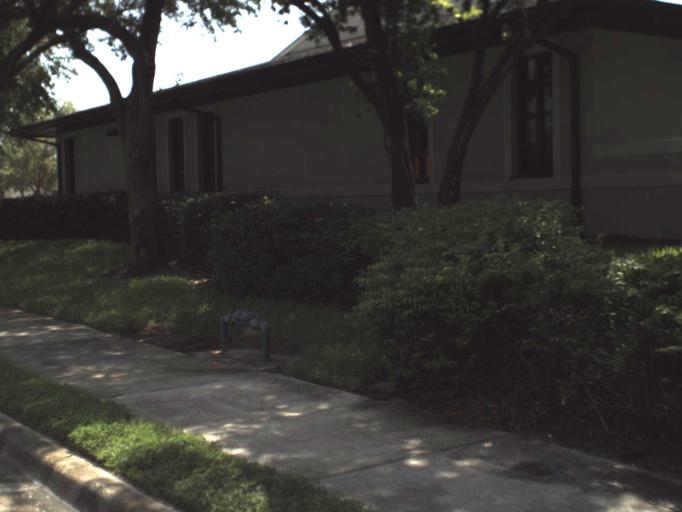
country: US
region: Florida
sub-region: Pinellas County
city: Kenneth City
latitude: 27.8325
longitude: -82.7286
